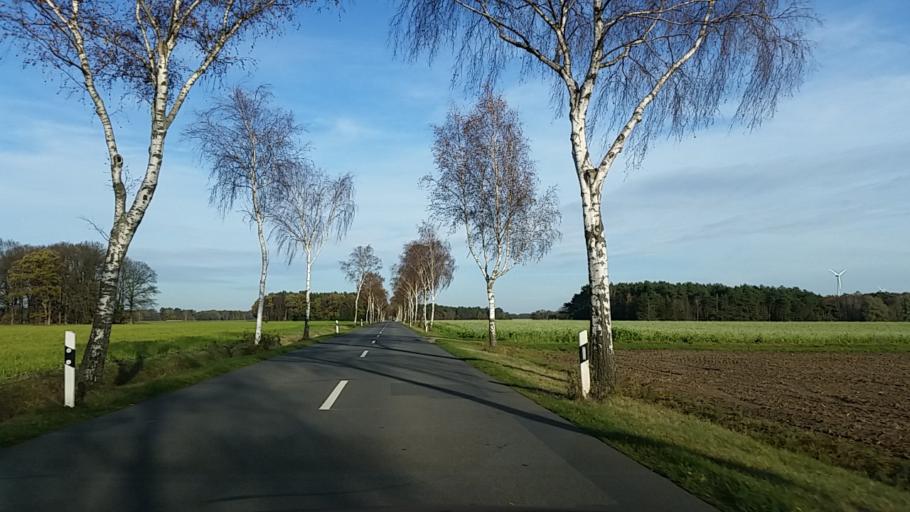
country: DE
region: Lower Saxony
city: Gross Oesingen
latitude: 52.6603
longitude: 10.4999
